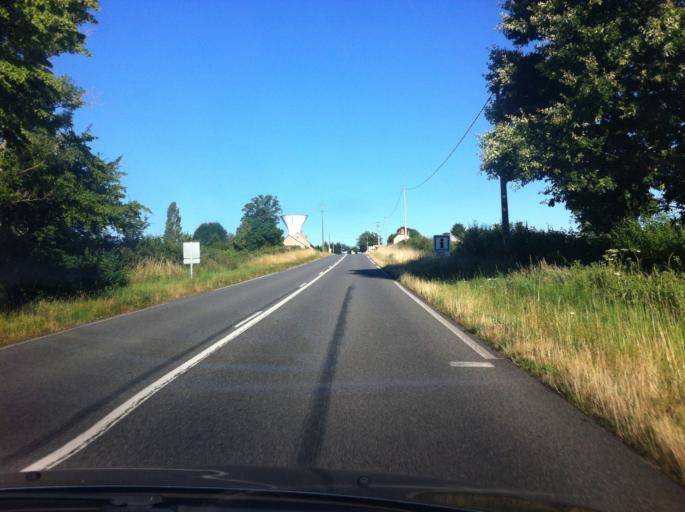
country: FR
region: Auvergne
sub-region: Departement de l'Allier
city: Montmarault
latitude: 46.3252
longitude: 3.0680
